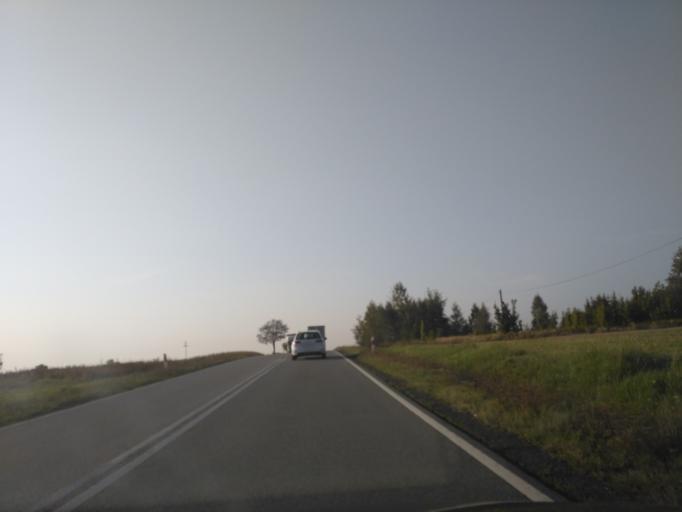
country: PL
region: Lublin Voivodeship
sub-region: Powiat janowski
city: Modliborzyce
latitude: 50.7882
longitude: 22.3192
